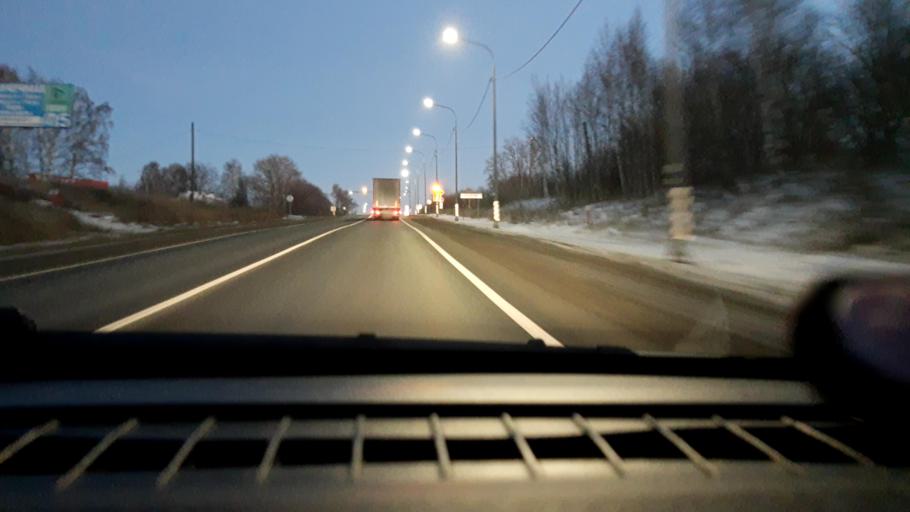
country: RU
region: Nizjnij Novgorod
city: Lyskovo
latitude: 56.0160
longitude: 45.0052
